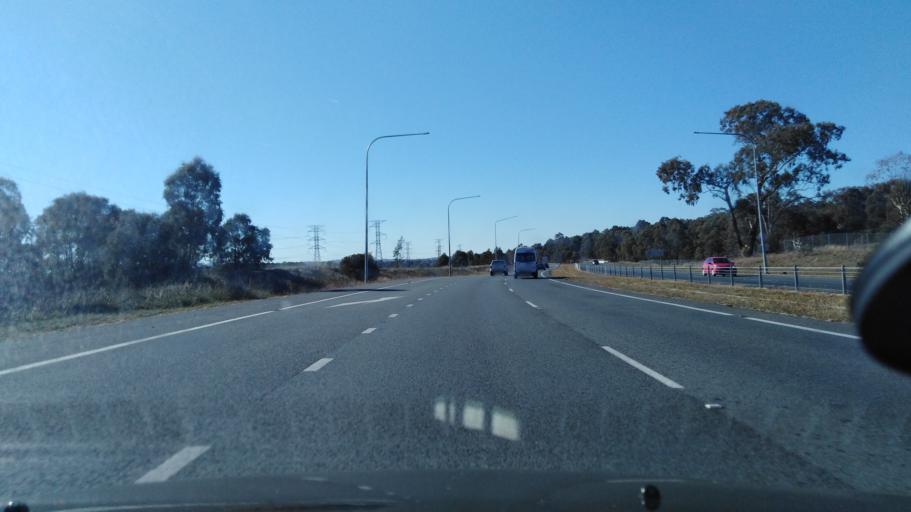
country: AU
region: Australian Capital Territory
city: Kaleen
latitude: -35.2389
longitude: 149.1124
